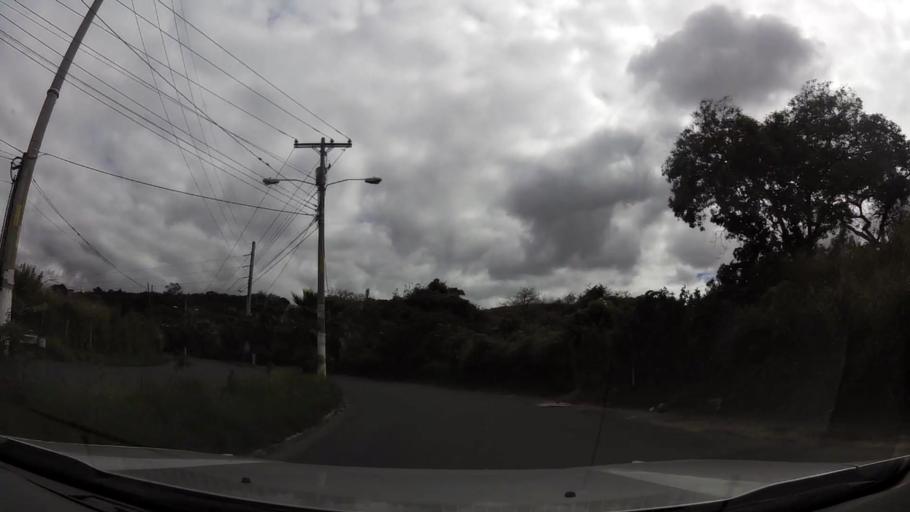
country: GT
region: Guatemala
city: Guatemala City
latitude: 14.6718
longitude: -90.5570
